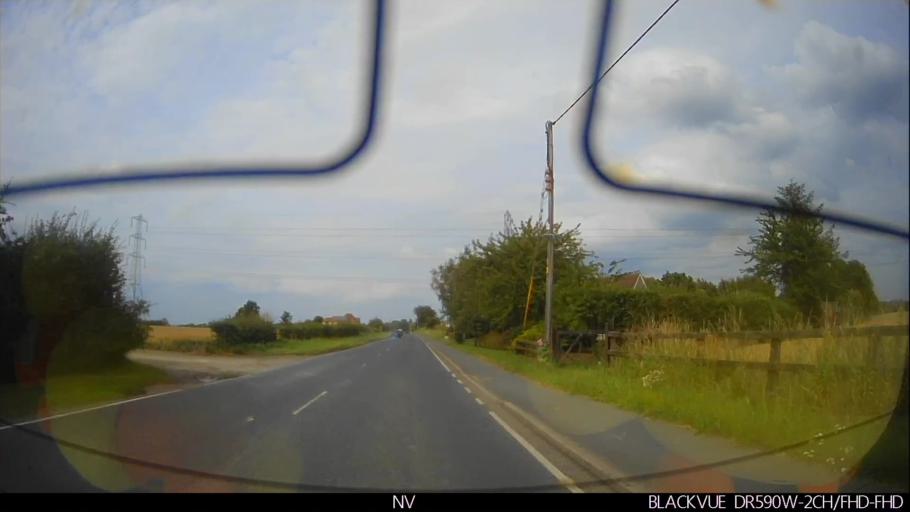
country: GB
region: England
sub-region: City of York
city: Huntington
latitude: 54.0141
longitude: -1.0505
